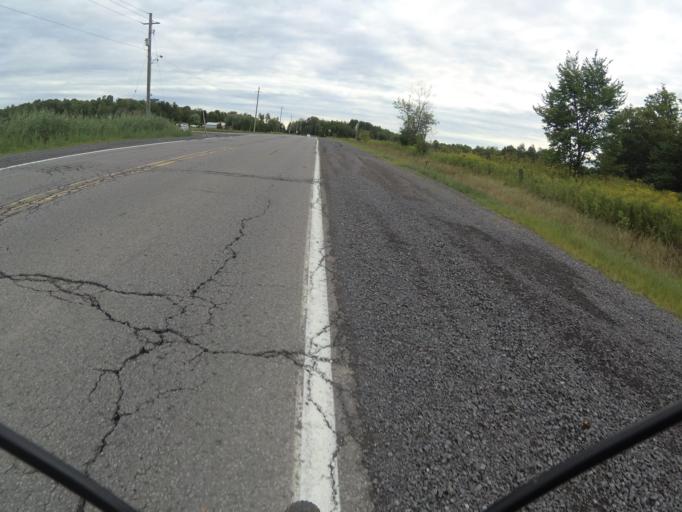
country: CA
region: Ontario
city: Bourget
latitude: 45.3957
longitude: -75.2814
